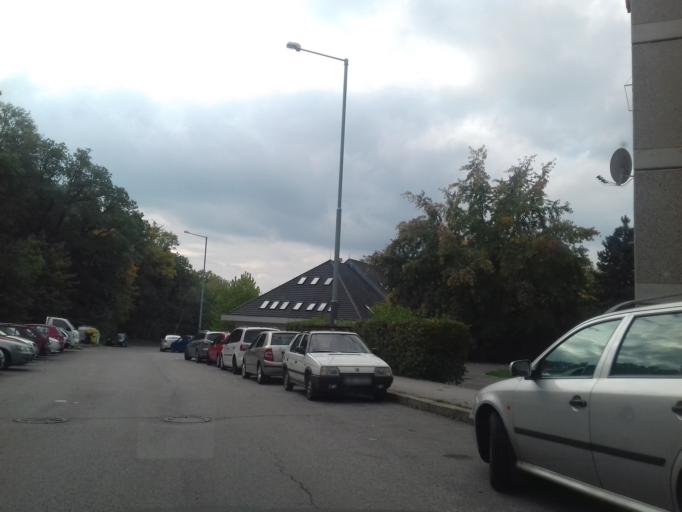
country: CZ
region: Praha
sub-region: Praha 4
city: Hodkovicky
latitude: 50.0209
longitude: 14.4110
